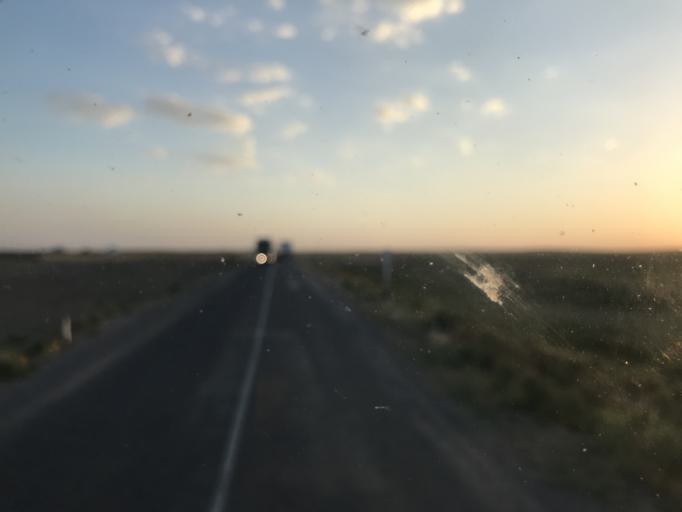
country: UZ
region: Toshkent
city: Yangiyul
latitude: 41.3843
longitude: 68.7661
